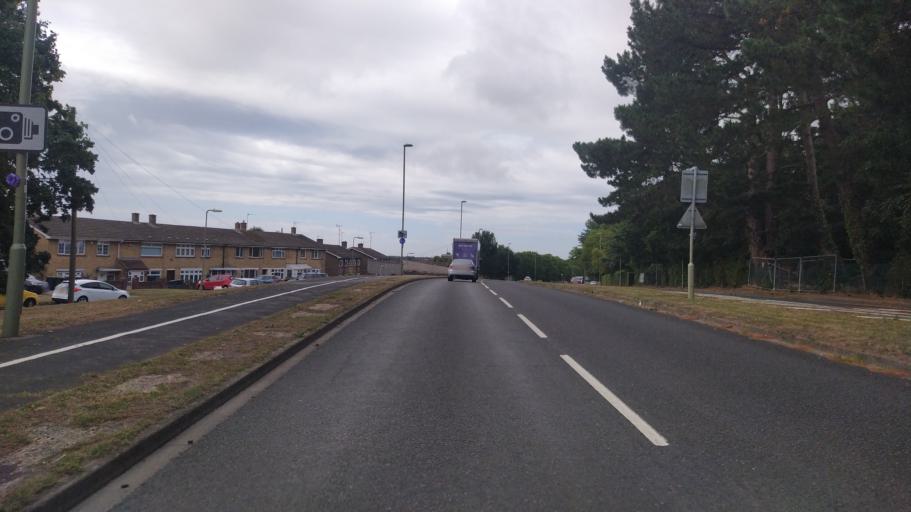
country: GB
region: England
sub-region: Hampshire
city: Havant
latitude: 50.8729
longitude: -0.9737
